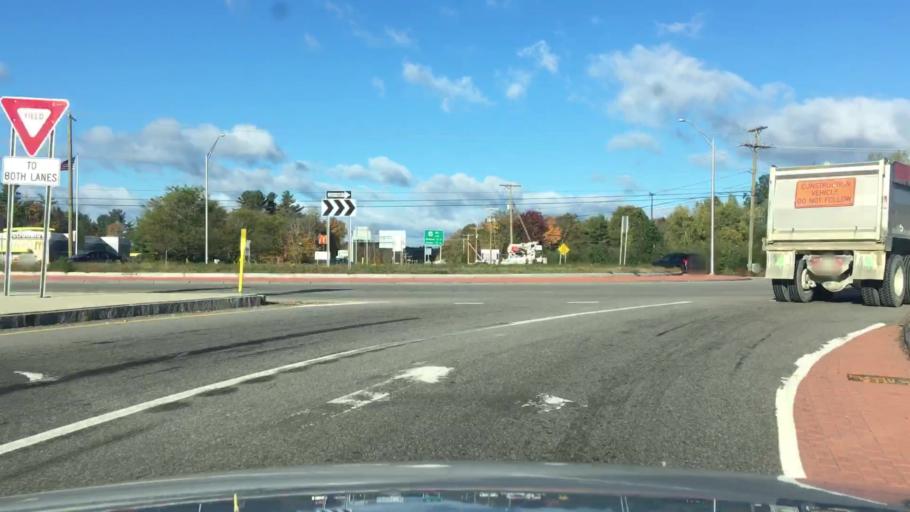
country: US
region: New Hampshire
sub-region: Strafford County
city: Lee
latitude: 43.1491
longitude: -71.0061
